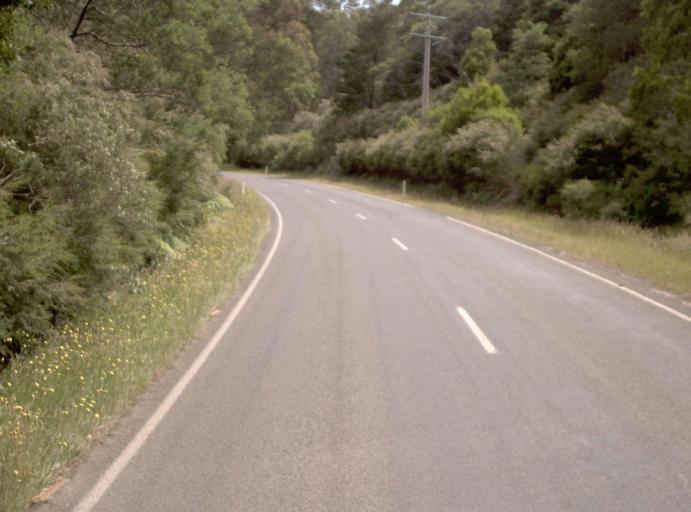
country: AU
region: Victoria
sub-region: Latrobe
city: Moe
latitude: -37.9384
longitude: 146.4028
